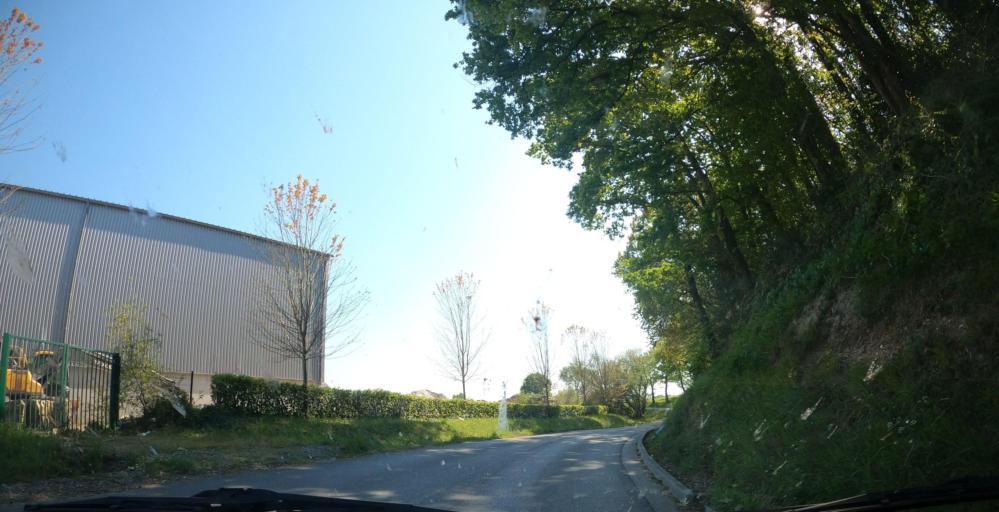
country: FR
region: Aquitaine
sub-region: Departement des Pyrenees-Atlantiques
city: Bassussarry
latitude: 43.4493
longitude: -1.4970
